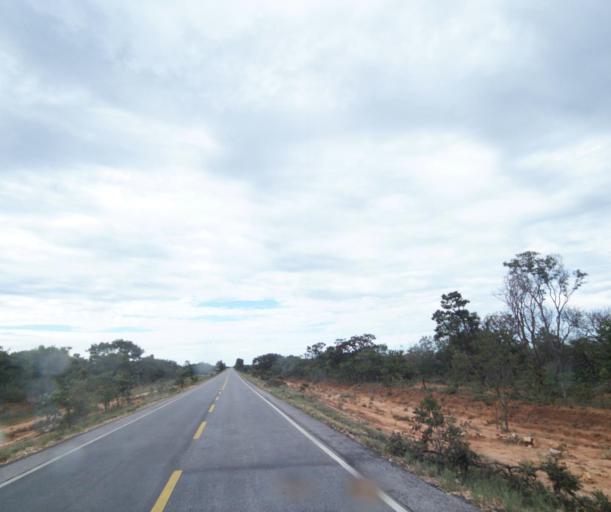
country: BR
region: Bahia
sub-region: Sao Felix Do Coribe
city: Santa Maria da Vitoria
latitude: -13.9752
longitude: -44.4463
